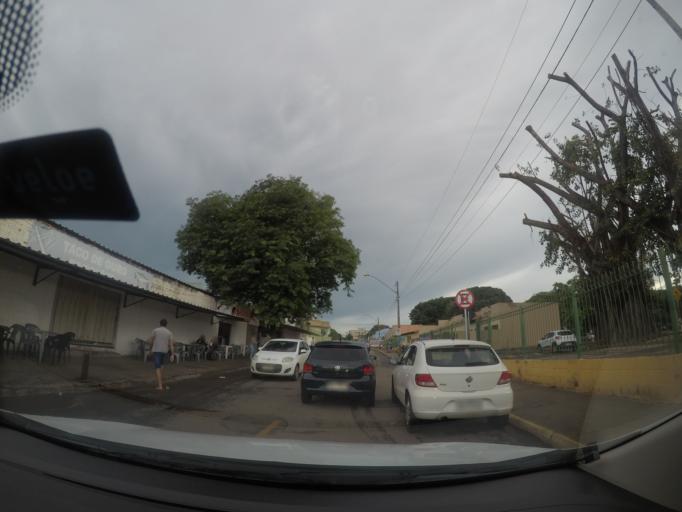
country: BR
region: Goias
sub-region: Goiania
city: Goiania
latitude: -16.6909
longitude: -49.3085
